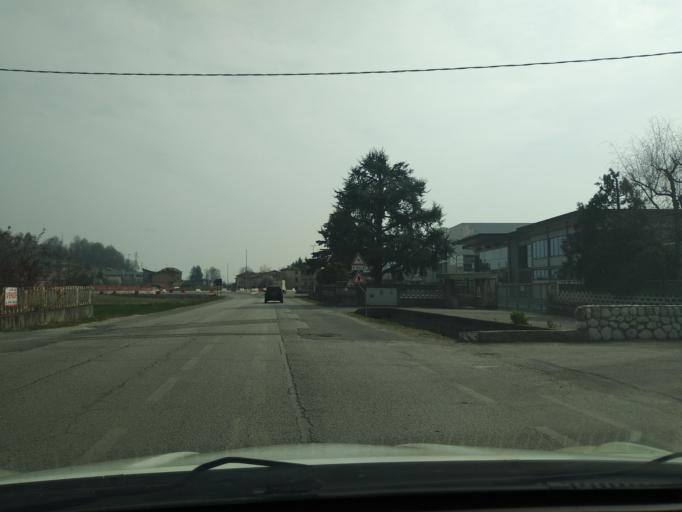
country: IT
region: Veneto
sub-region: Provincia di Vicenza
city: Chiampo
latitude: 45.5319
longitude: 11.3065
